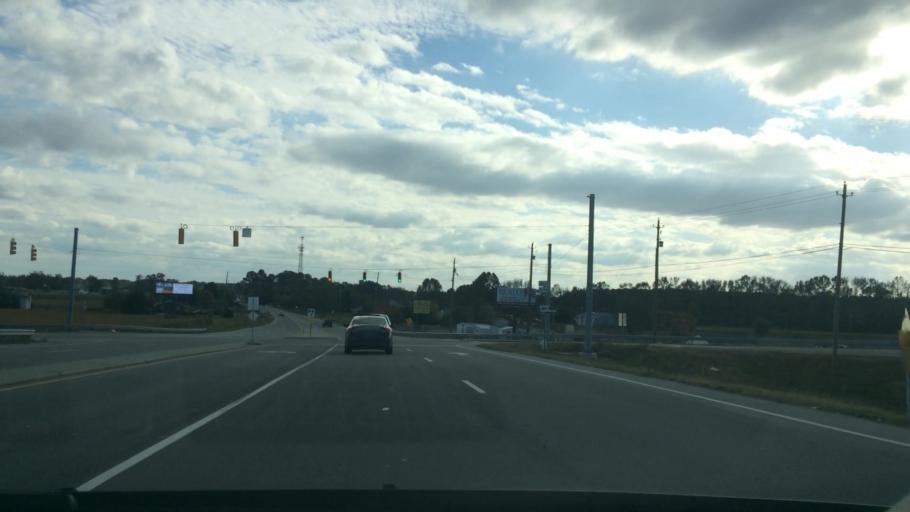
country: US
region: North Carolina
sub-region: Wayne County
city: Elroy
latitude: 35.4117
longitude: -77.8975
